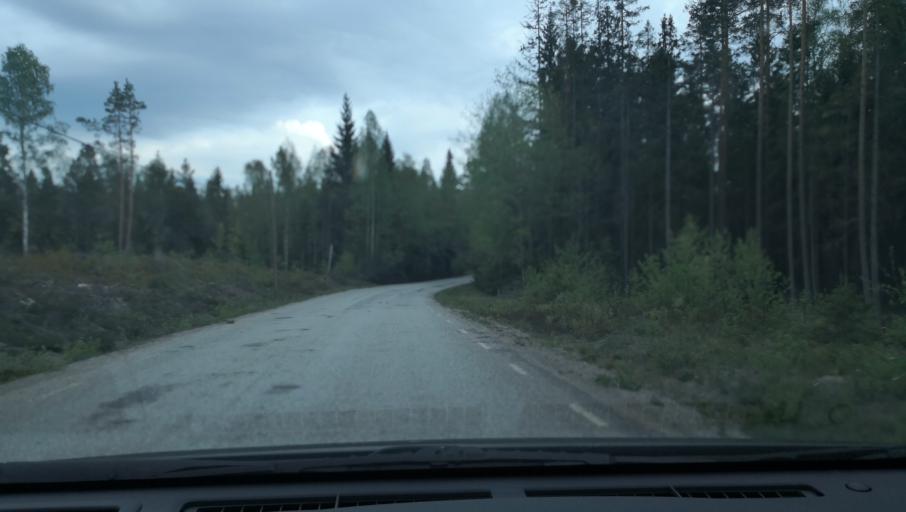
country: SE
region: Vaestmanland
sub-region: Skinnskattebergs Kommun
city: Skinnskatteberg
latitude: 59.8202
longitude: 15.5517
